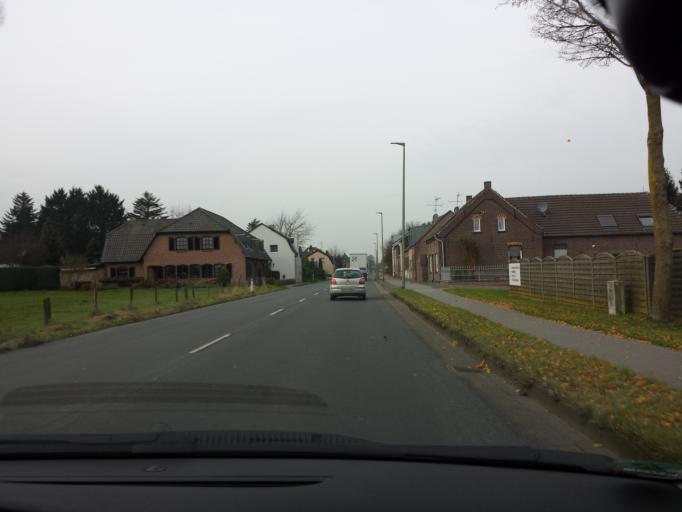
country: DE
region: North Rhine-Westphalia
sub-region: Regierungsbezirk Dusseldorf
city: Goch
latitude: 51.6821
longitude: 6.1414
